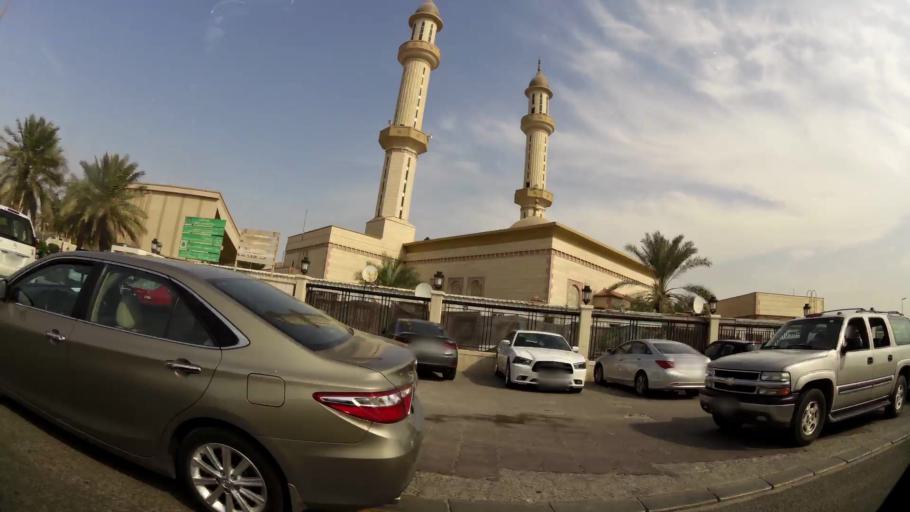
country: KW
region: Al Asimah
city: Ash Shamiyah
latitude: 29.3193
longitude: 47.9695
